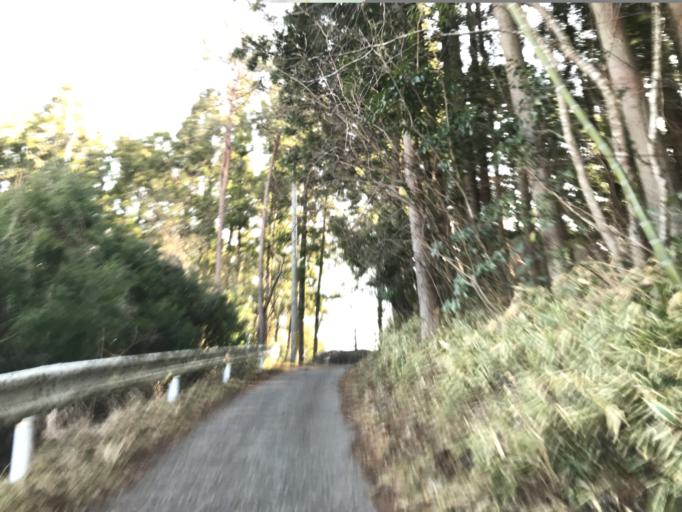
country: JP
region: Fukushima
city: Iwaki
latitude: 37.0502
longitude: 140.7921
